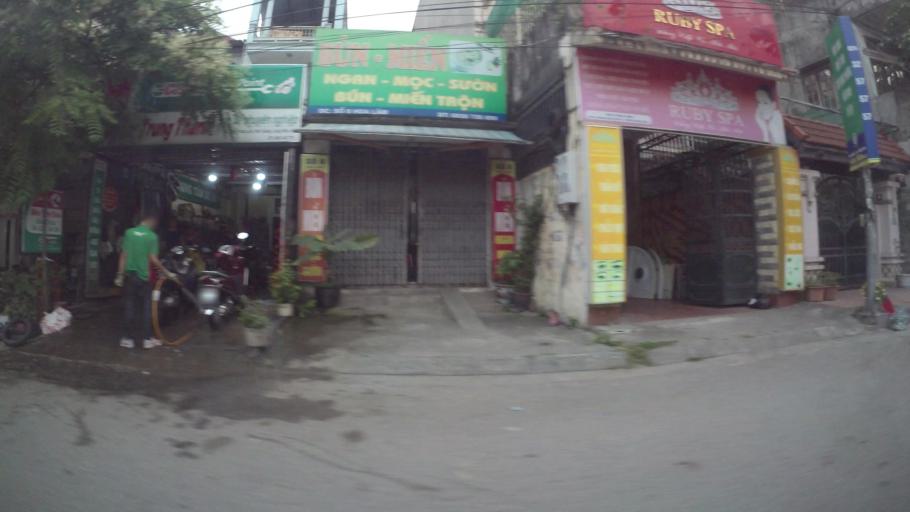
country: VN
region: Ha Noi
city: Hoan Kiem
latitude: 21.0601
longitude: 105.8935
